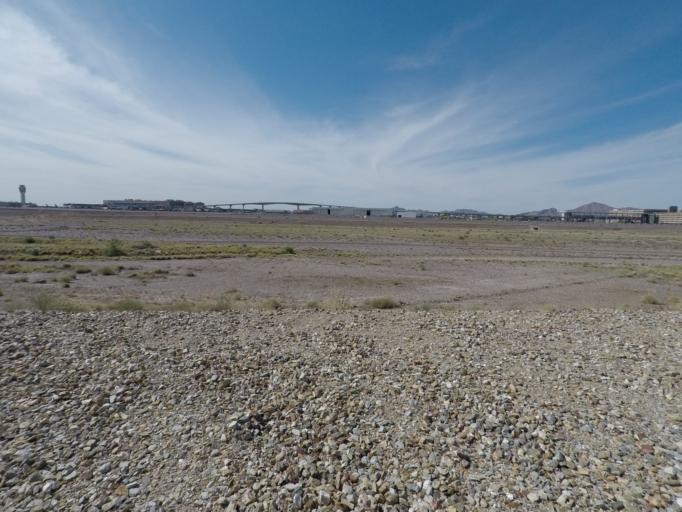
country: US
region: Arizona
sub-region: Maricopa County
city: Tempe Junction
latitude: 33.4280
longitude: -111.9872
